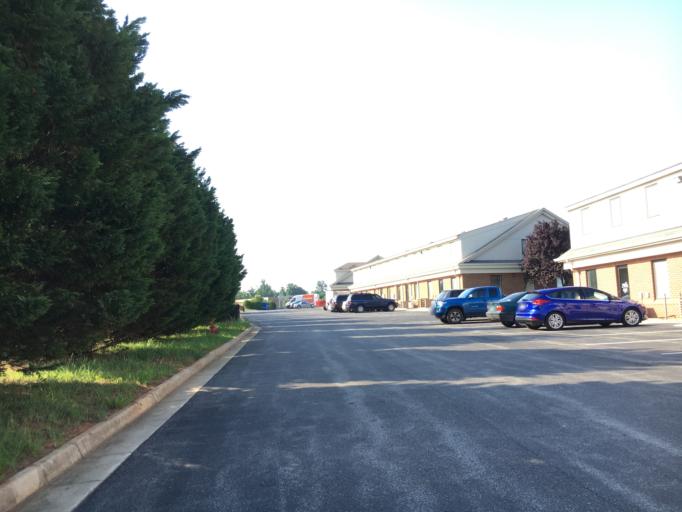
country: US
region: Virginia
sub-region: Bedford County
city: Forest
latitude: 37.3727
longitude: -79.2542
